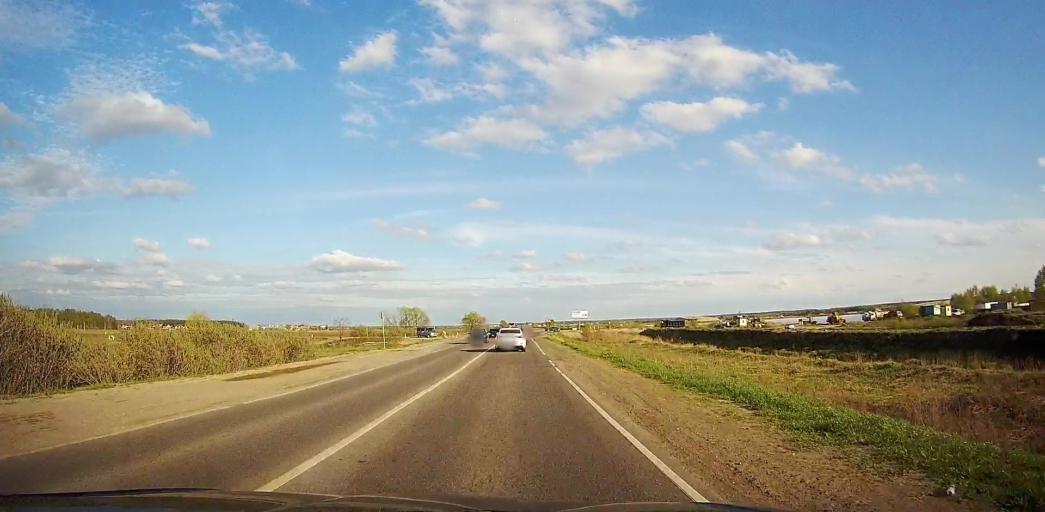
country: RU
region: Moskovskaya
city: Ramenskoye
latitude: 55.5131
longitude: 38.2779
